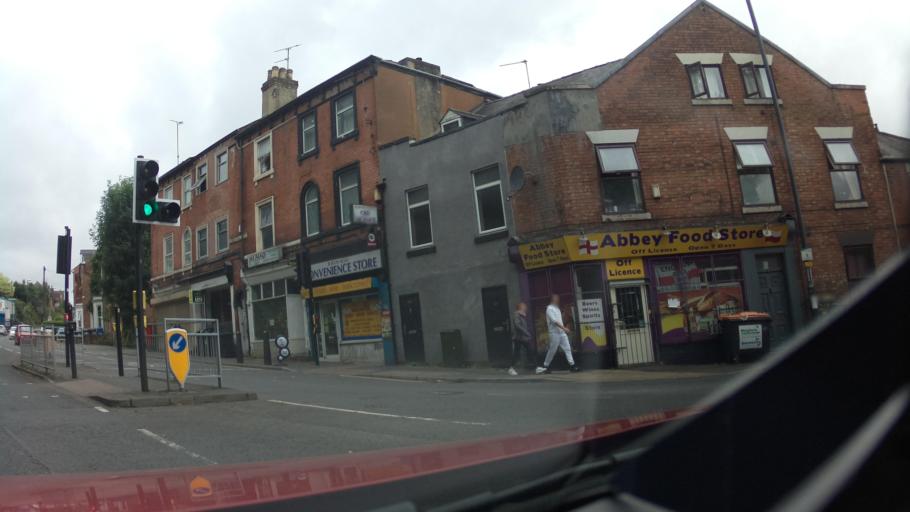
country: GB
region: England
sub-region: Derby
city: Derby
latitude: 52.9139
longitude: -1.4832
